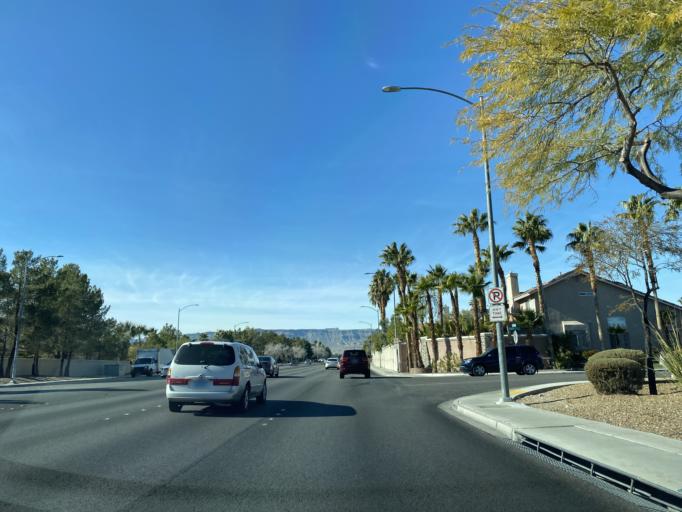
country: US
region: Nevada
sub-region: Clark County
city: Spring Valley
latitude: 36.1001
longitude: -115.2812
